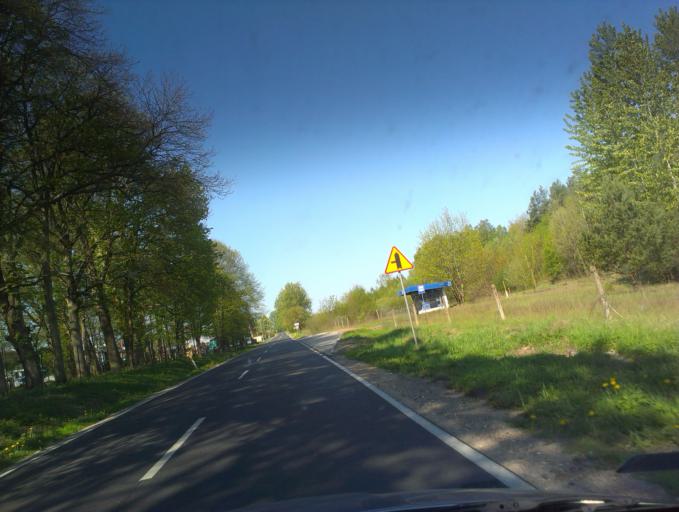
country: PL
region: West Pomeranian Voivodeship
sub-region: Powiat swidwinski
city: Polczyn-Zdroj
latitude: 53.7703
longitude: 16.1399
